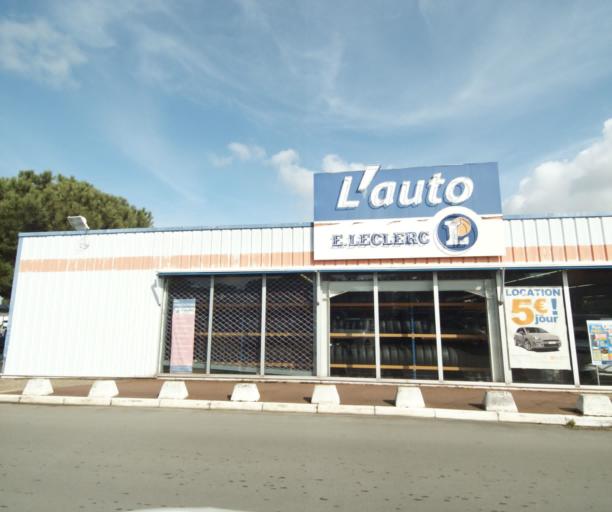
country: FR
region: Poitou-Charentes
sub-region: Departement de la Charente-Maritime
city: La Rochelle
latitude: 46.1743
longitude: -1.1678
